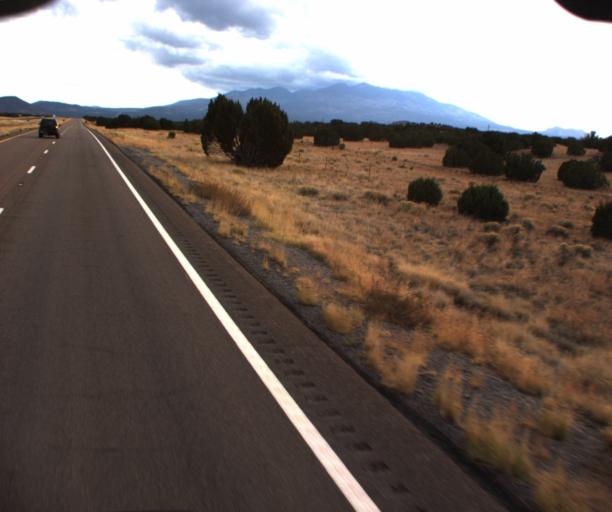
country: US
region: Arizona
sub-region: Coconino County
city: Flagstaff
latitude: 35.4869
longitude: -111.5557
